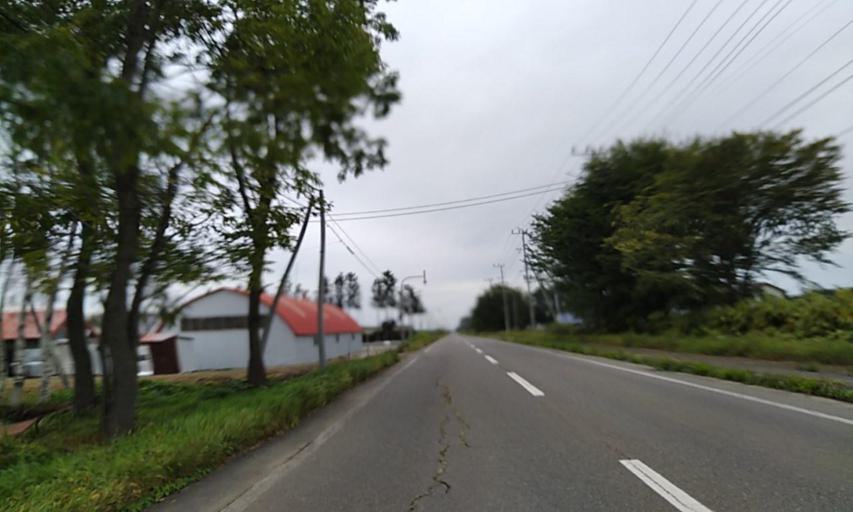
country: JP
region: Hokkaido
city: Obihiro
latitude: 42.6452
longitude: 143.0977
